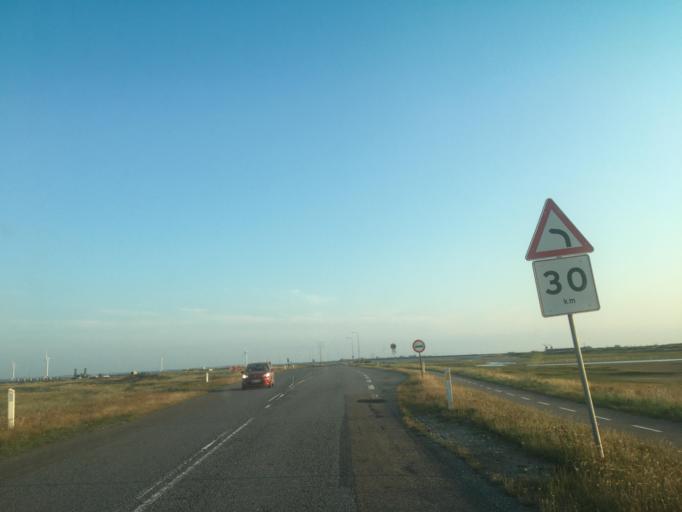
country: DK
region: Central Jutland
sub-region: Lemvig Kommune
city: Thyboron
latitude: 56.7059
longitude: 8.2470
